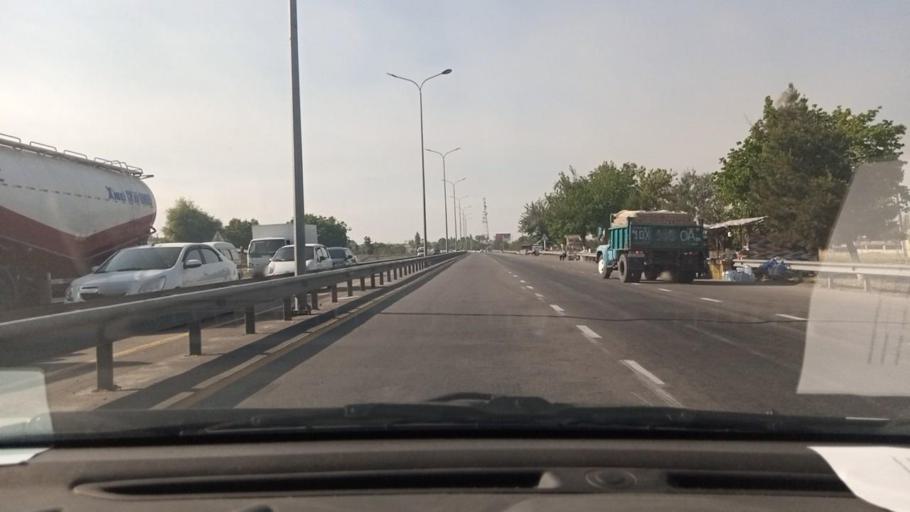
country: UZ
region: Toshkent
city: Tuytepa
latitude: 41.1302
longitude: 69.4363
